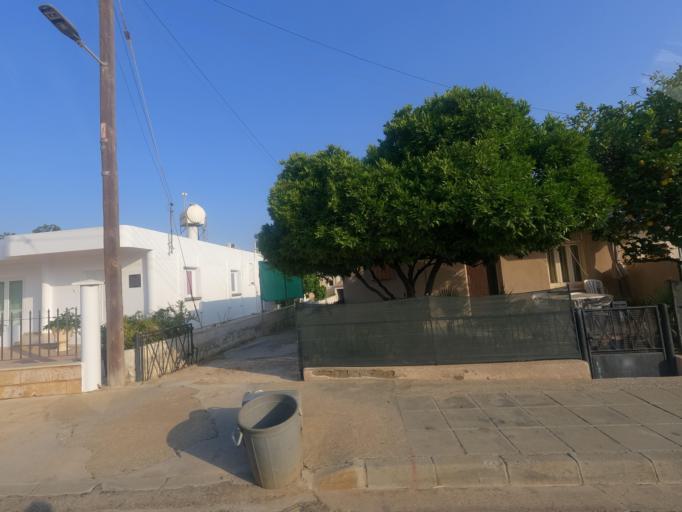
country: CY
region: Ammochostos
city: Achna
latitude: 35.0318
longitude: 33.7699
